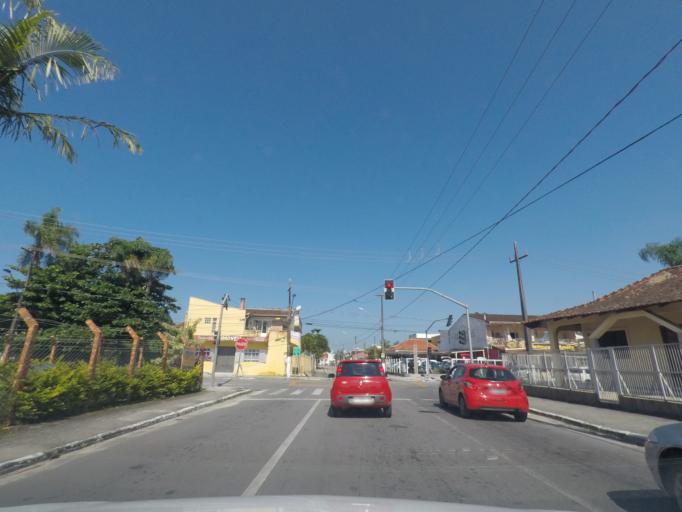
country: BR
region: Parana
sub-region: Guaratuba
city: Guaratuba
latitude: -25.8162
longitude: -48.5366
